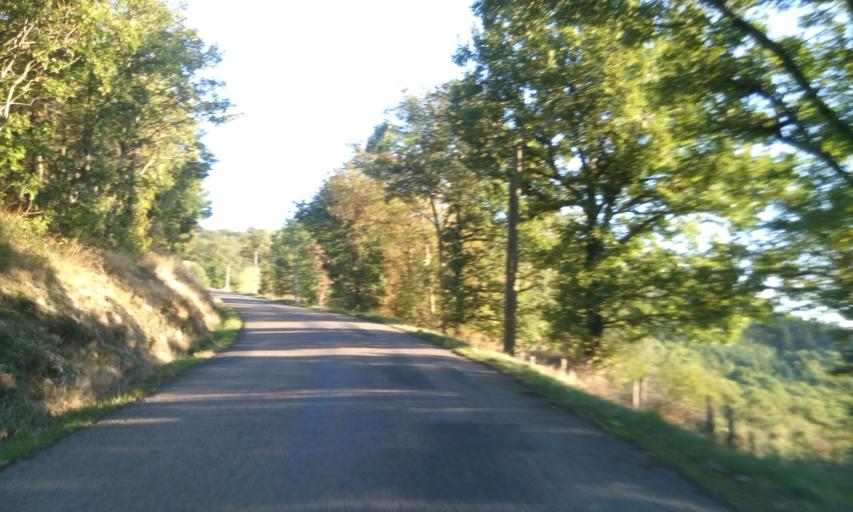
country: FR
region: Rhone-Alpes
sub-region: Departement du Rhone
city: Tarare
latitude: 45.9522
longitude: 4.4431
